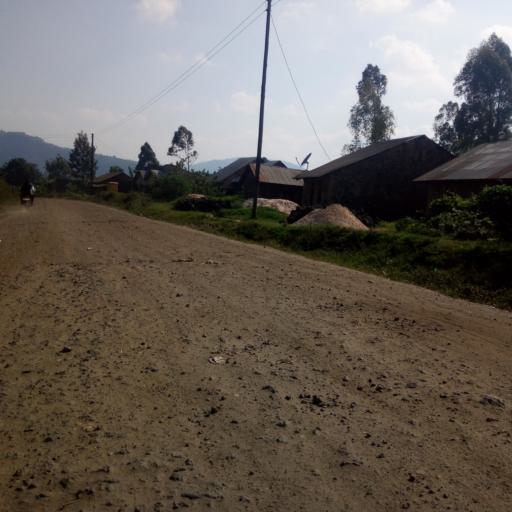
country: UG
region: Western Region
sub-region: Kisoro District
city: Kisoro
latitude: -1.2348
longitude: 29.7125
